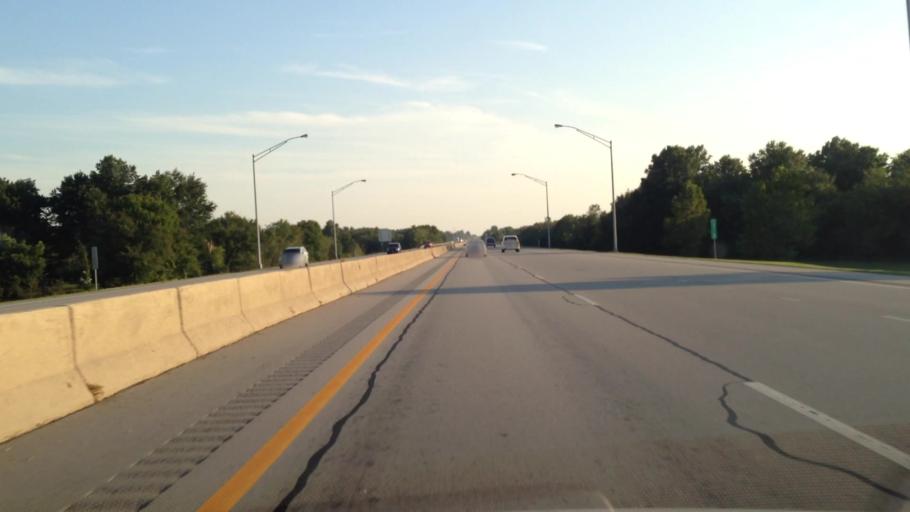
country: US
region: Oklahoma
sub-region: Ottawa County
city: Miami
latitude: 36.8618
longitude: -94.8516
